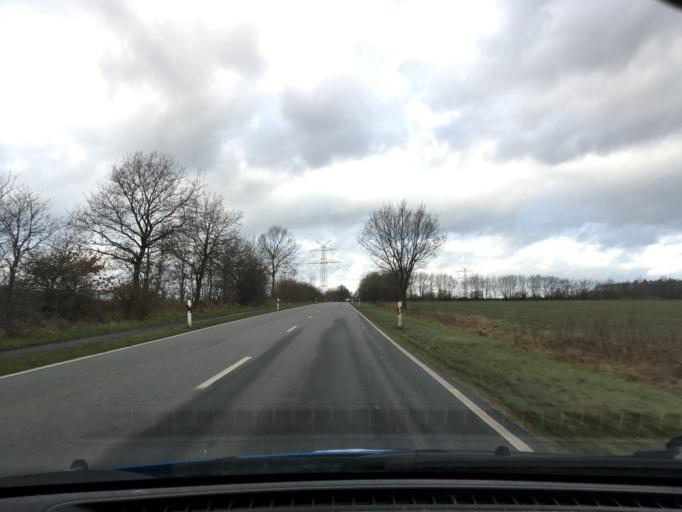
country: DE
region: Schleswig-Holstein
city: Kaisborstel
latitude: 54.0061
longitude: 9.4863
